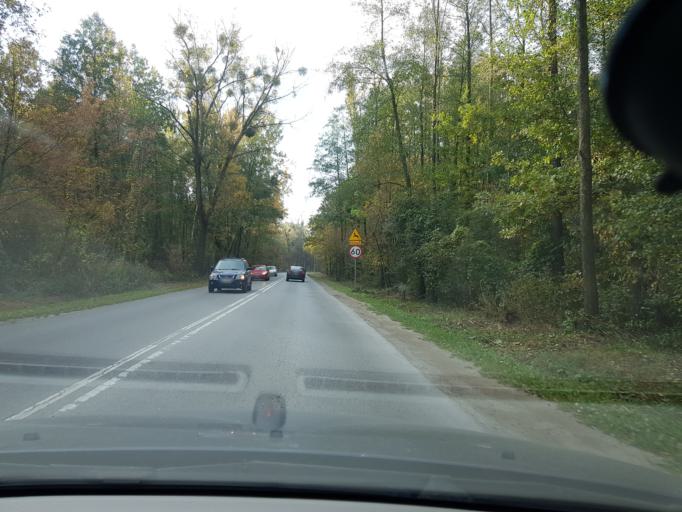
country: PL
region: Masovian Voivodeship
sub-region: Powiat warszawski zachodni
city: Babice
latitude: 52.2746
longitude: 20.8752
